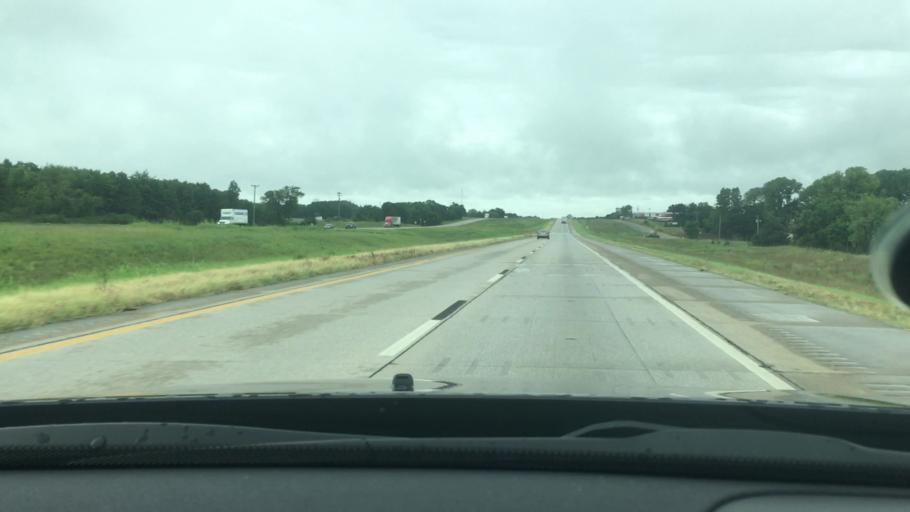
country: US
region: Oklahoma
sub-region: Atoka County
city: Atoka
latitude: 34.2035
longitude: -96.2373
